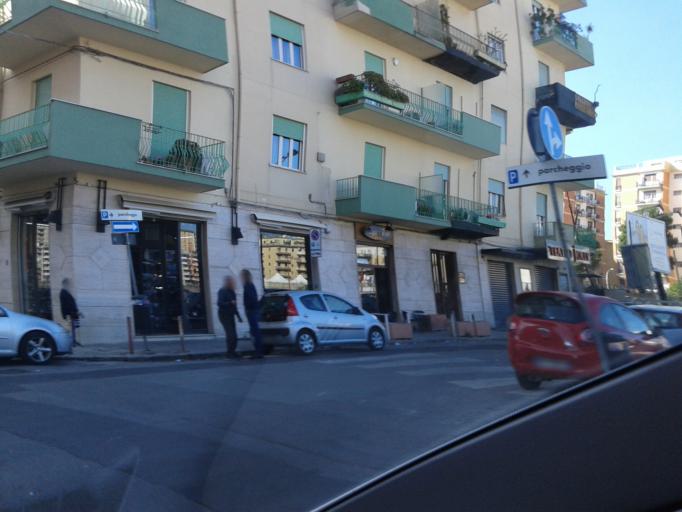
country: IT
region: Sicily
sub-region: Palermo
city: Palermo
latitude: 38.1310
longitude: 13.3430
